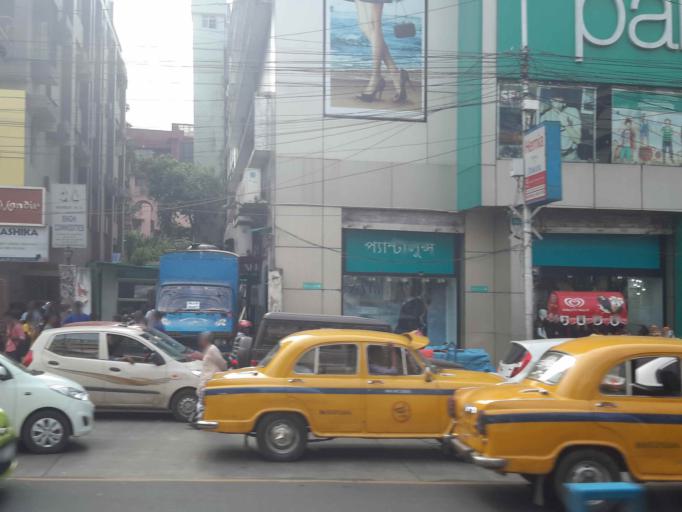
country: IN
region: West Bengal
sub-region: Kolkata
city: Kolkata
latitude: 22.5230
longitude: 88.3653
